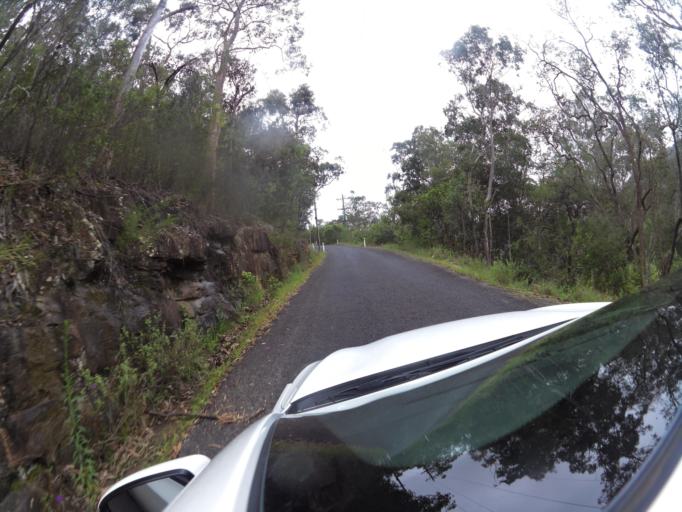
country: AU
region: New South Wales
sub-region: Hornsby Shire
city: Glenorie
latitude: -33.4282
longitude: 150.9554
